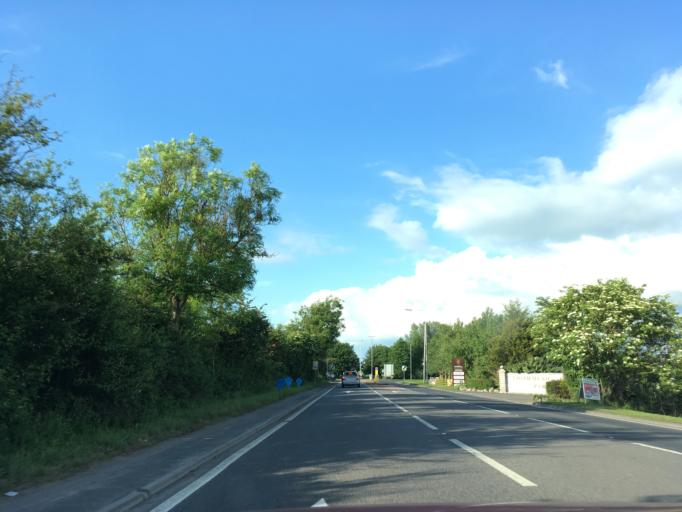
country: GB
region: England
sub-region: Somerset
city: Highbridge
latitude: 51.2360
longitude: -2.9537
